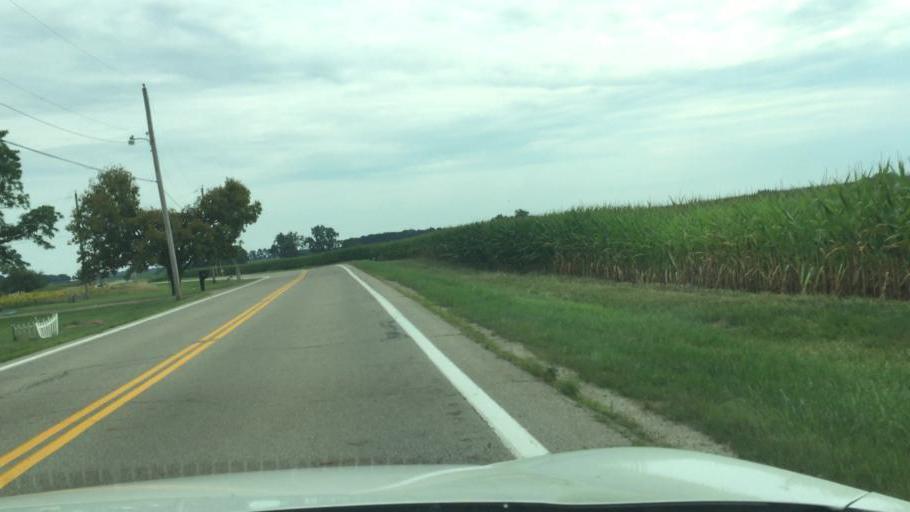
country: US
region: Ohio
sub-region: Champaign County
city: North Lewisburg
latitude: 40.1694
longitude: -83.5278
